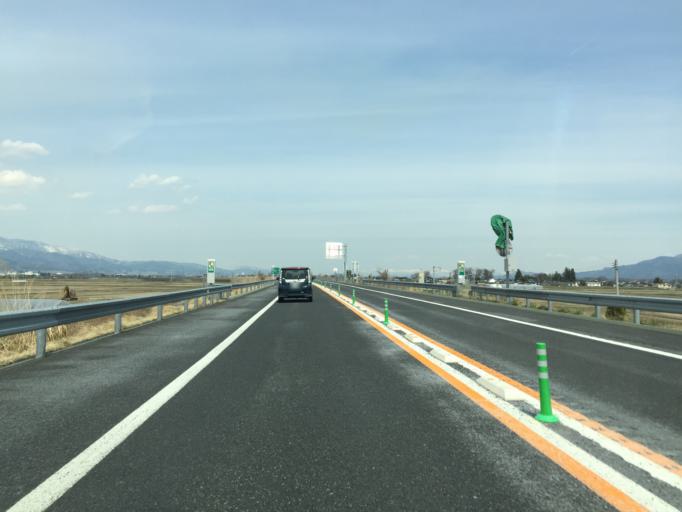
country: JP
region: Yamagata
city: Tendo
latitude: 38.3730
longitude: 140.3470
